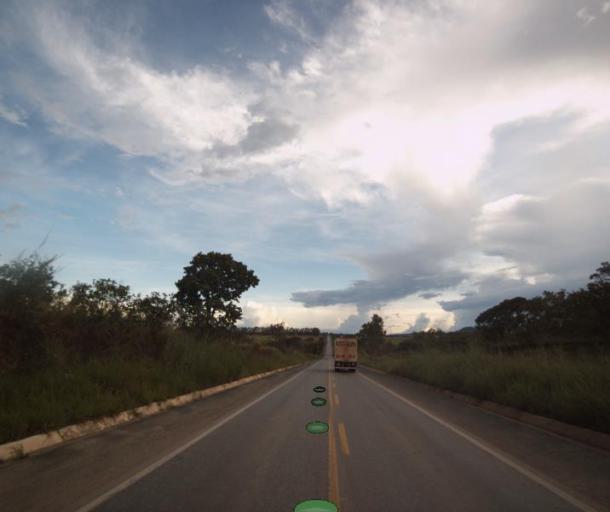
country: BR
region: Goias
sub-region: Uruacu
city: Uruacu
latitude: -14.1304
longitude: -49.1112
